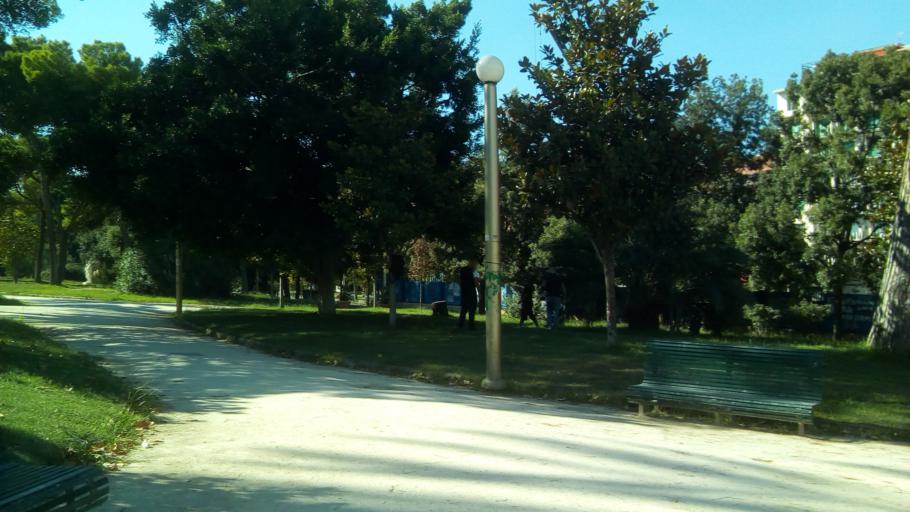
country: IT
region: Campania
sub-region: Provincia di Napoli
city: Napoli
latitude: 40.8320
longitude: 14.2407
